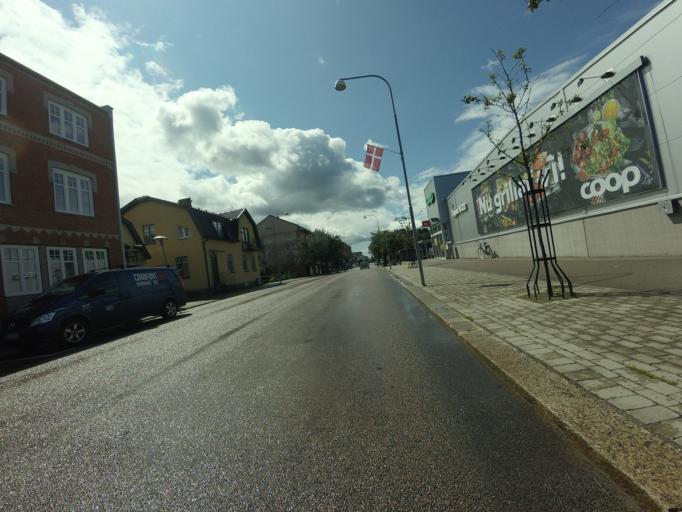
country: SE
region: Skane
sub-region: Osby Kommun
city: Osby
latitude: 56.3833
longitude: 13.9952
